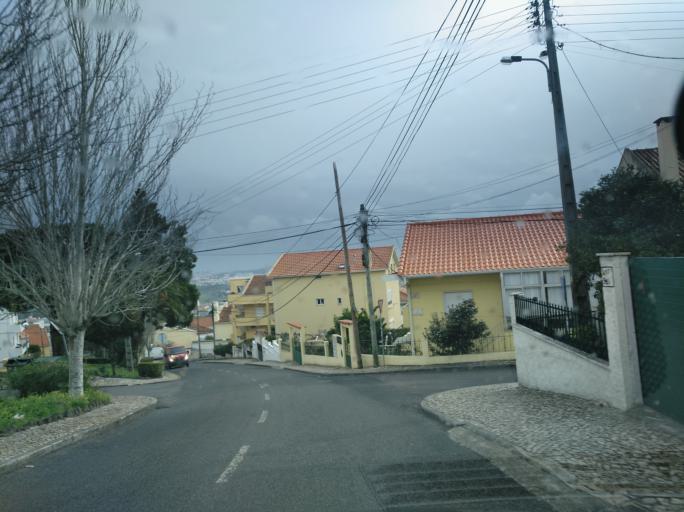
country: PT
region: Lisbon
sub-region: Odivelas
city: Famoes
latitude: 38.7949
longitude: -9.2166
